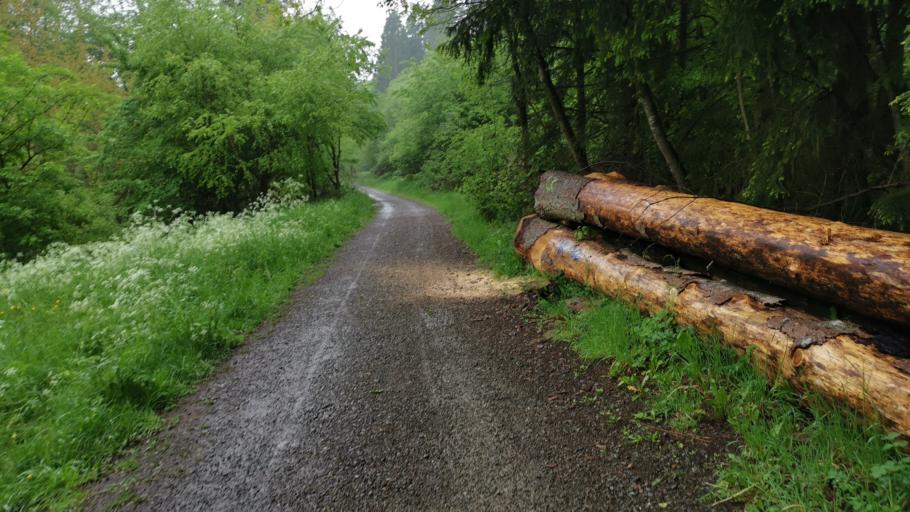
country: DE
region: Saarland
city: Kirkel
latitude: 49.2597
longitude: 7.1867
